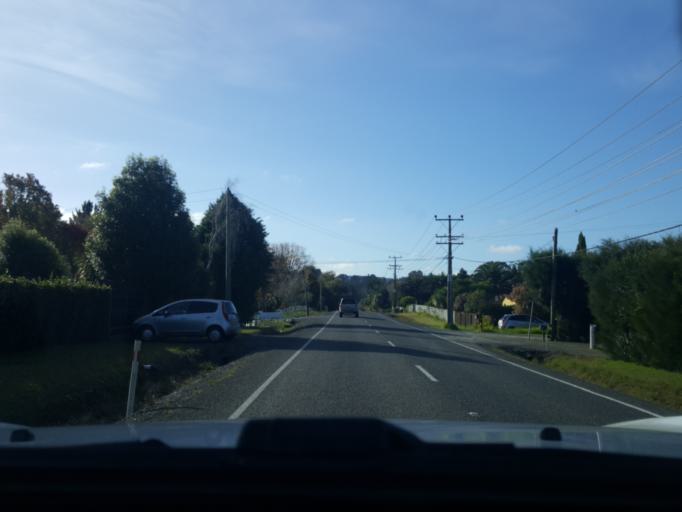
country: NZ
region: Auckland
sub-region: Auckland
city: Muriwai Beach
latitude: -36.7670
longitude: 174.5764
